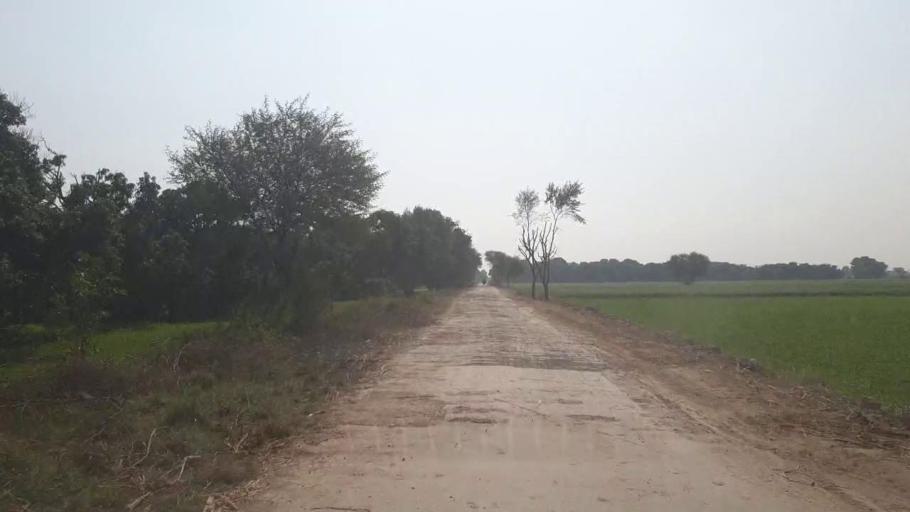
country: PK
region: Sindh
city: Tando Allahyar
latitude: 25.4816
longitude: 68.8260
